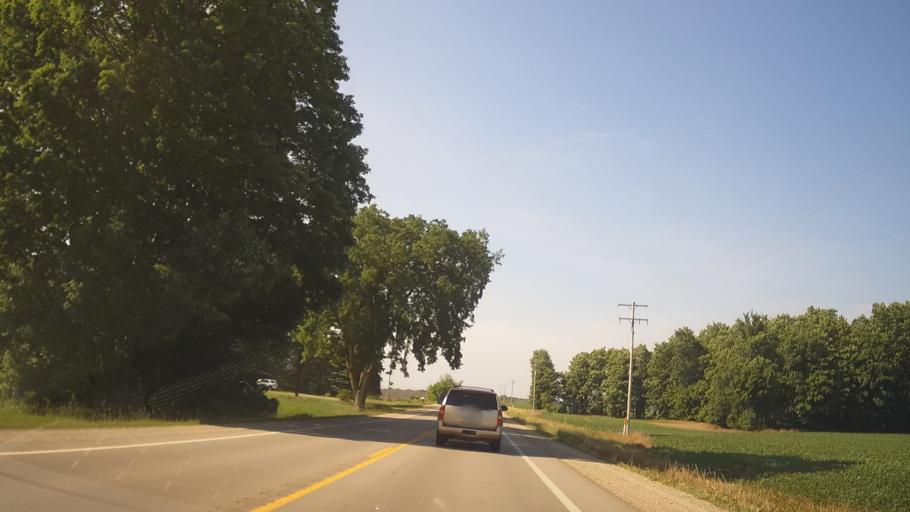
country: US
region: Michigan
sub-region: Ogemaw County
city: West Branch
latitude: 44.3145
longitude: -84.1257
